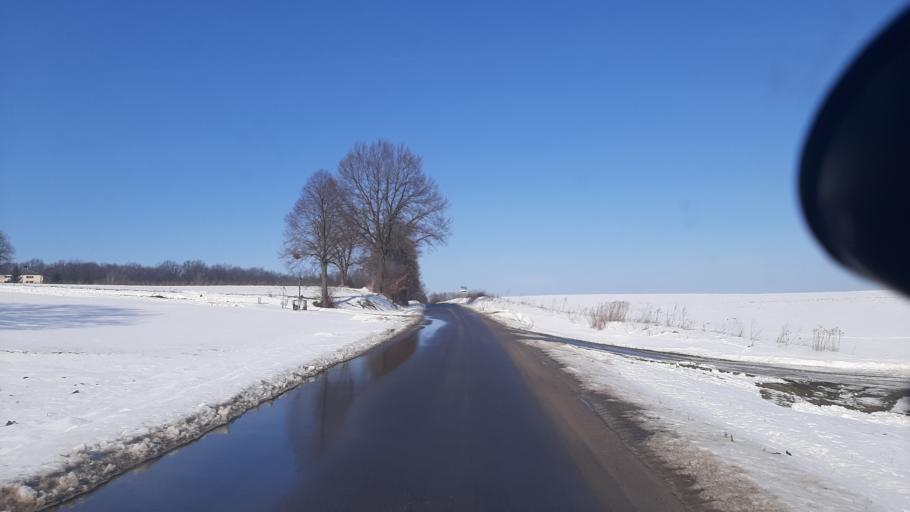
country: PL
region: Lublin Voivodeship
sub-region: Powiat pulawski
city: Naleczow
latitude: 51.2912
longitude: 22.2709
